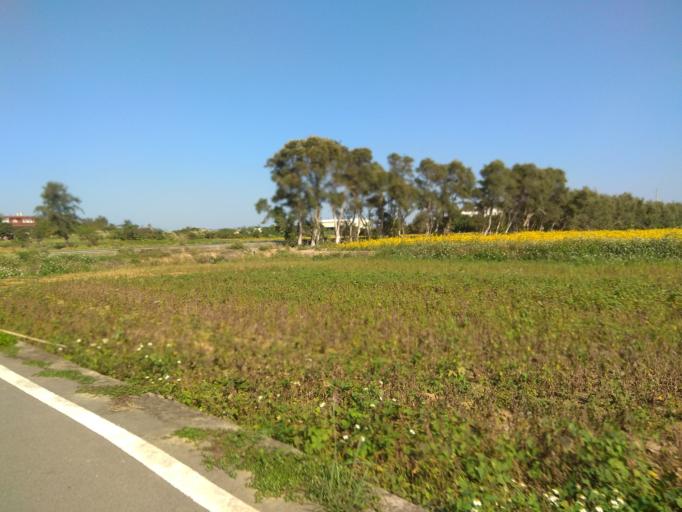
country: TW
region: Taiwan
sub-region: Hsinchu
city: Zhubei
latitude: 24.9903
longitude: 121.0341
